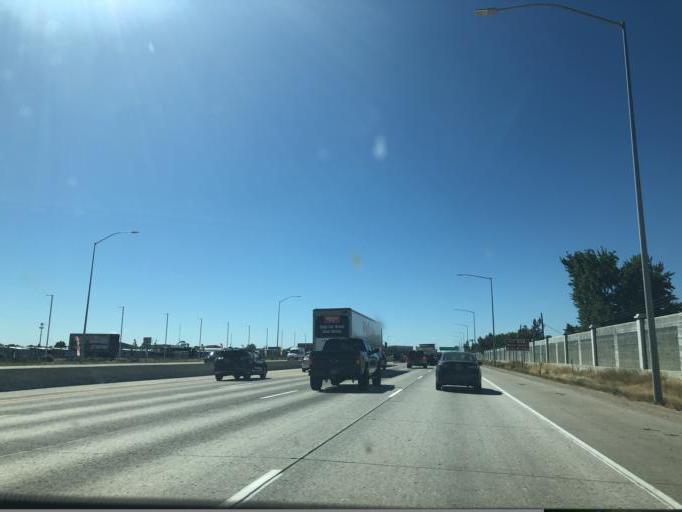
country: US
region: Idaho
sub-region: Ada County
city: Garden City
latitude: 43.5852
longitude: -116.2636
